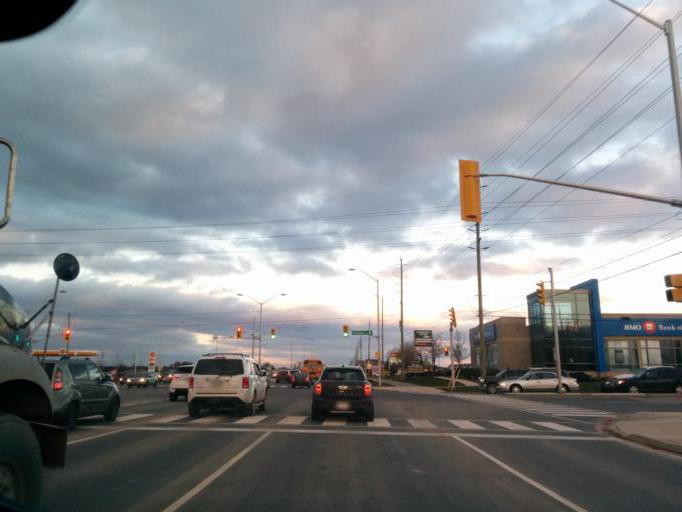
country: CA
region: Ontario
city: Oakville
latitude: 43.4875
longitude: -79.7198
